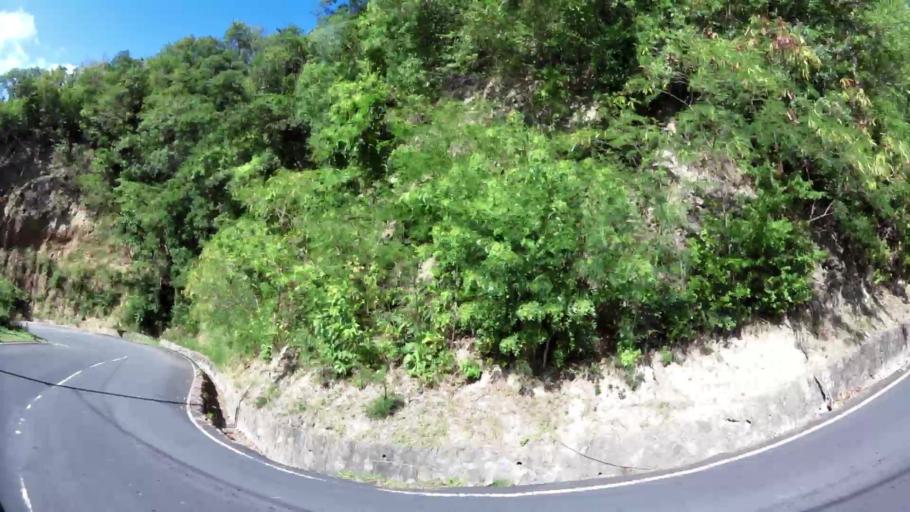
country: LC
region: Soufriere
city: Soufriere
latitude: 13.8620
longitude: -61.0525
